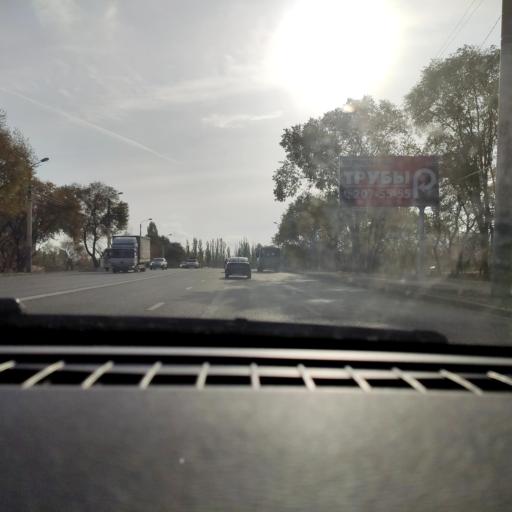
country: RU
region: Voronezj
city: Voronezh
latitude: 51.6233
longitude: 39.2341
